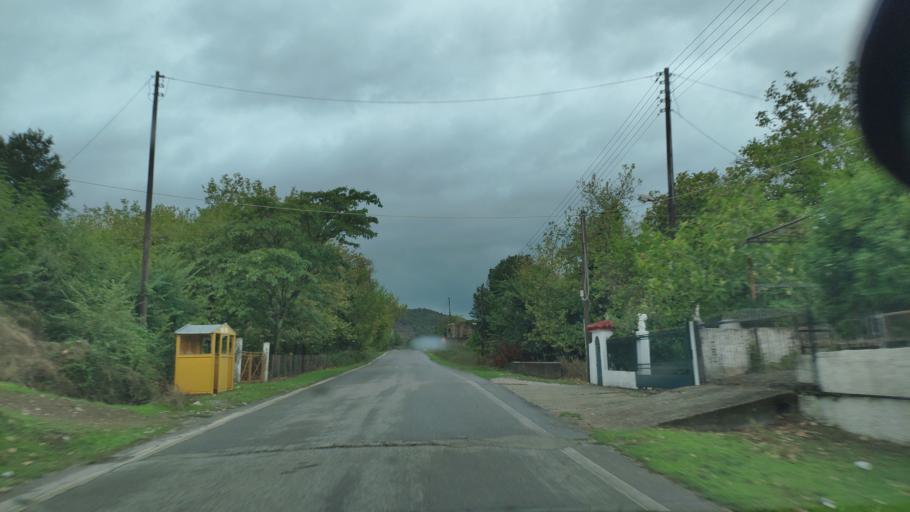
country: GR
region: West Greece
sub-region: Nomos Aitolias kai Akarnanias
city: Krikellos
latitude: 39.0004
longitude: 21.3104
